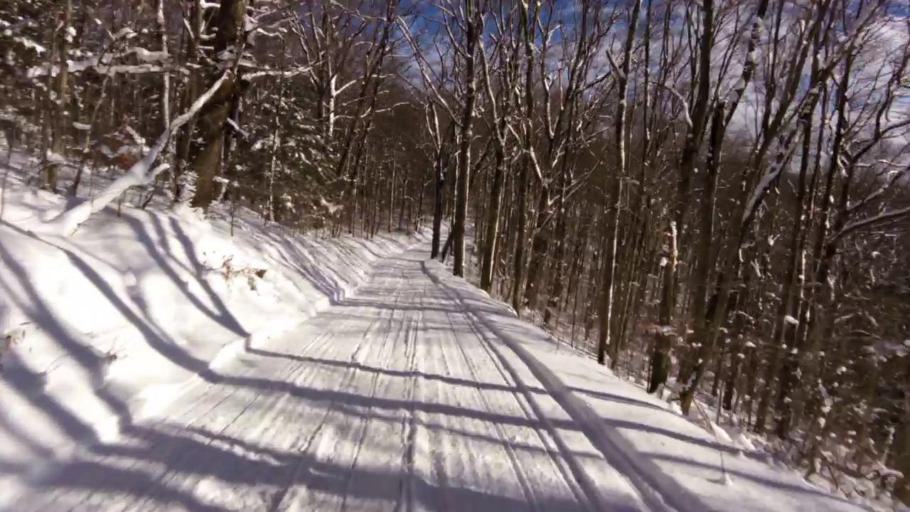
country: US
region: New York
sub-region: Cattaraugus County
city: Salamanca
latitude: 42.0714
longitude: -78.6798
